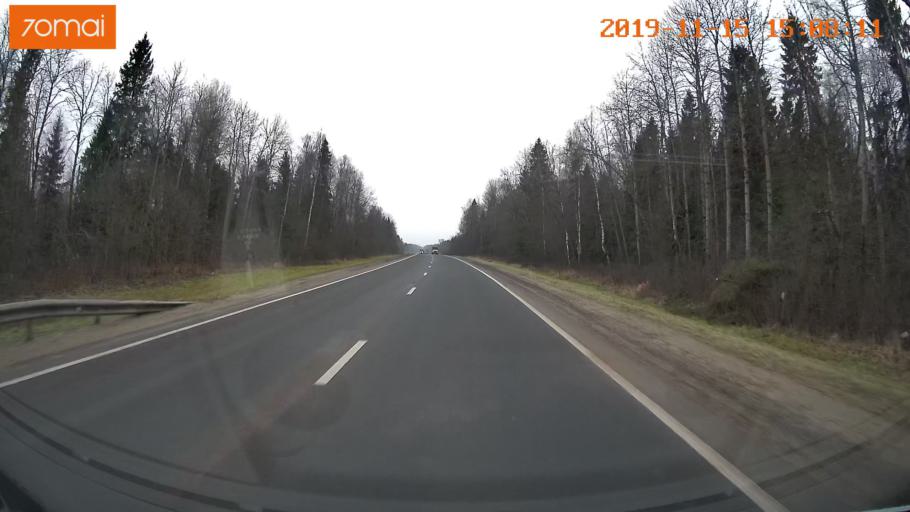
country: RU
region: Jaroslavl
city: Prechistoye
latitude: 58.3745
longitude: 40.2802
